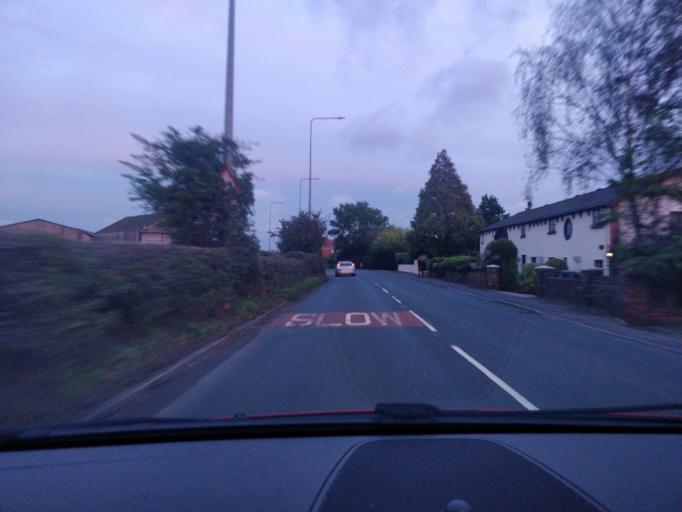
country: GB
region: England
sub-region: Sefton
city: Southport
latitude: 53.6189
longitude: -2.9499
